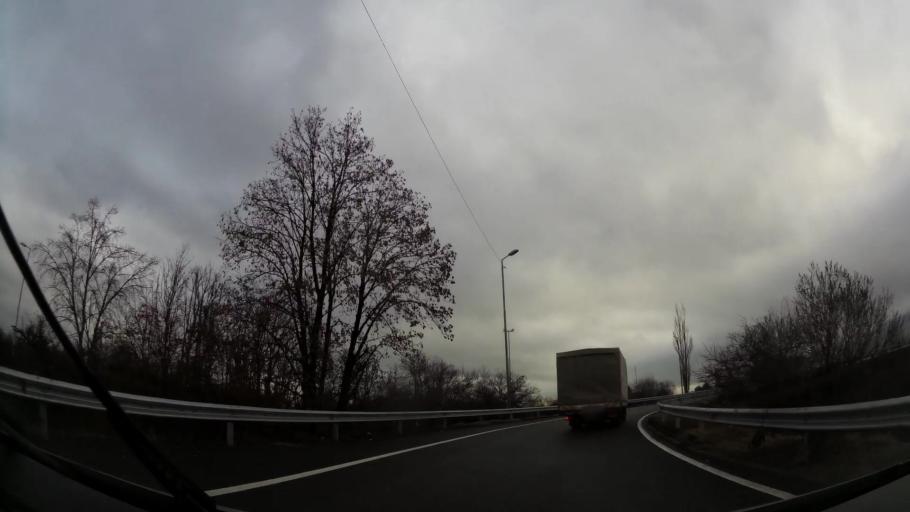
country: BG
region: Sofia-Capital
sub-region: Stolichna Obshtina
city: Sofia
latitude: 42.6345
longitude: 23.4473
